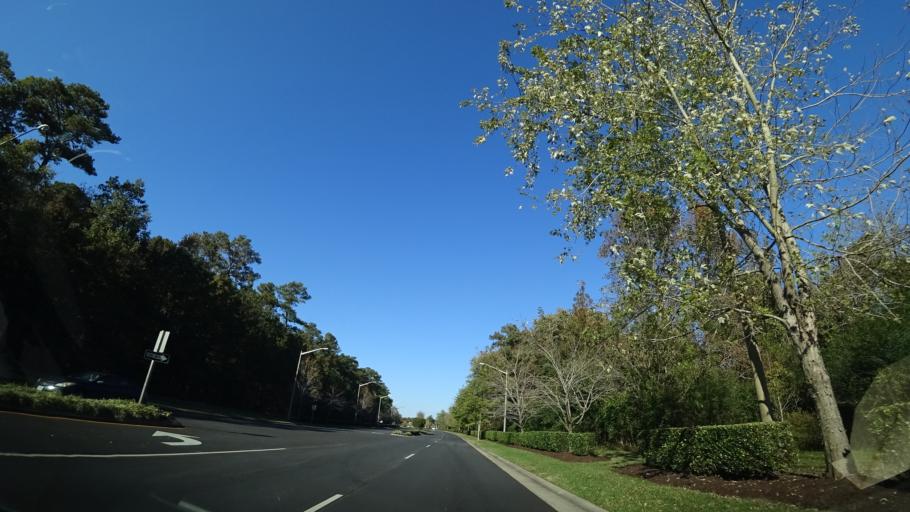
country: US
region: Virginia
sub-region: City of Portsmouth
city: Portsmouth Heights
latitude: 36.8803
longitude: -76.4372
